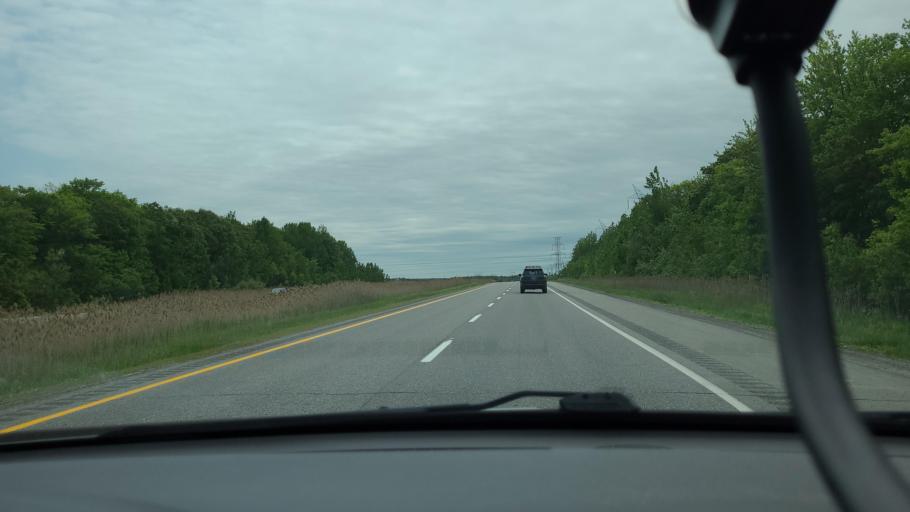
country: CA
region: Quebec
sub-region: Lanaudiere
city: Mascouche
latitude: 45.8013
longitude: -73.5875
